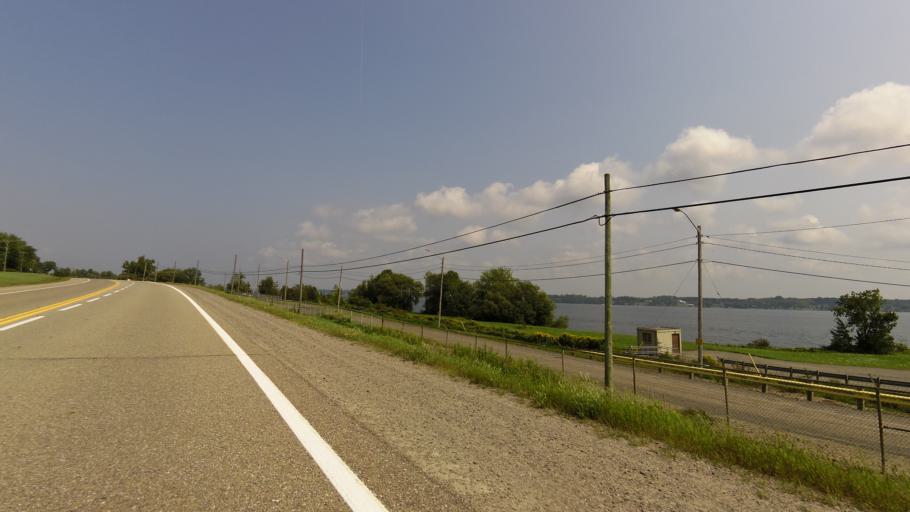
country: CA
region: Ontario
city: Prescott
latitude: 44.6590
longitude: -75.5796
